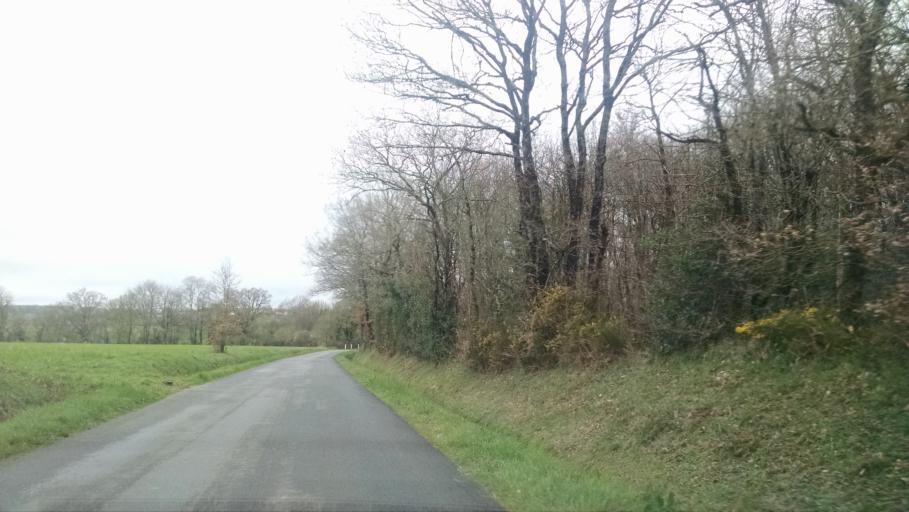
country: FR
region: Pays de la Loire
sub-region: Departement de la Loire-Atlantique
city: Vallet
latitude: 47.1893
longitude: -1.2660
